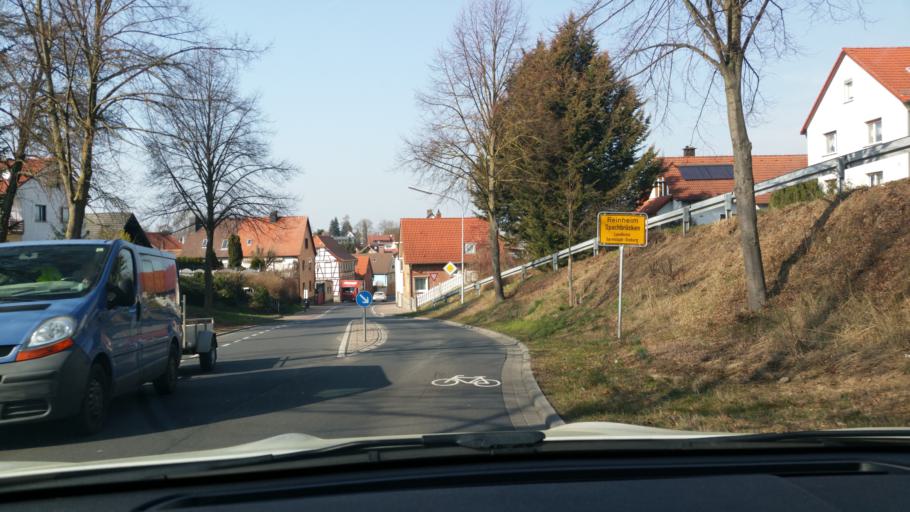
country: DE
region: Hesse
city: Reinheim
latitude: 49.8403
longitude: 8.8283
